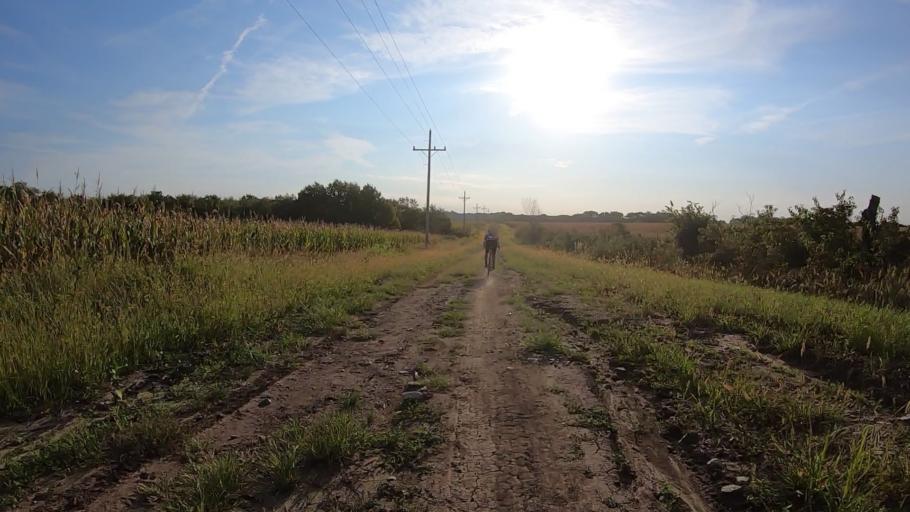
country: US
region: Kansas
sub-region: Marshall County
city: Blue Rapids
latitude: 39.7118
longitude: -96.7897
